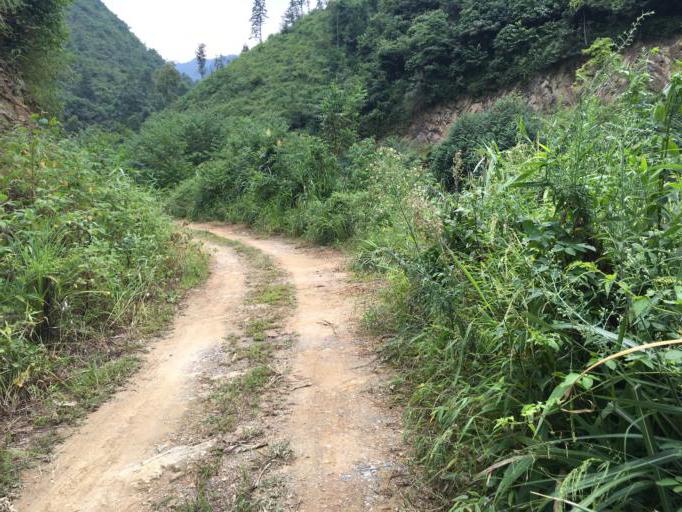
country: CN
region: Guangxi Zhuangzu Zizhiqu
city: Tongle
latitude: 25.2981
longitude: 106.1426
